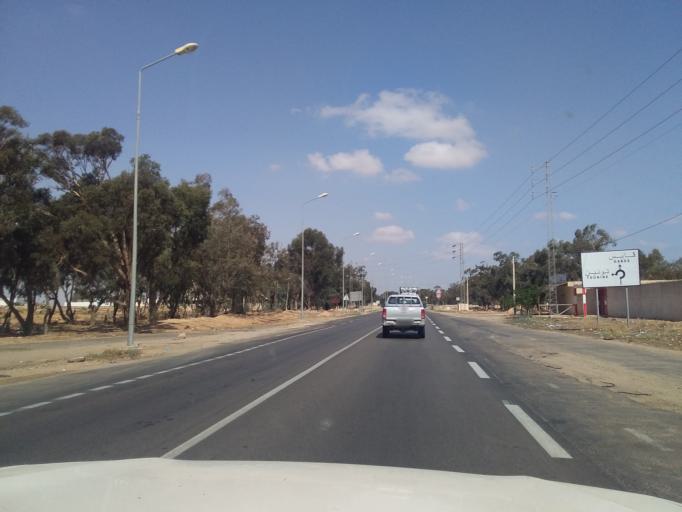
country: TN
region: Madanin
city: Medenine
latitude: 33.5970
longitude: 10.3104
